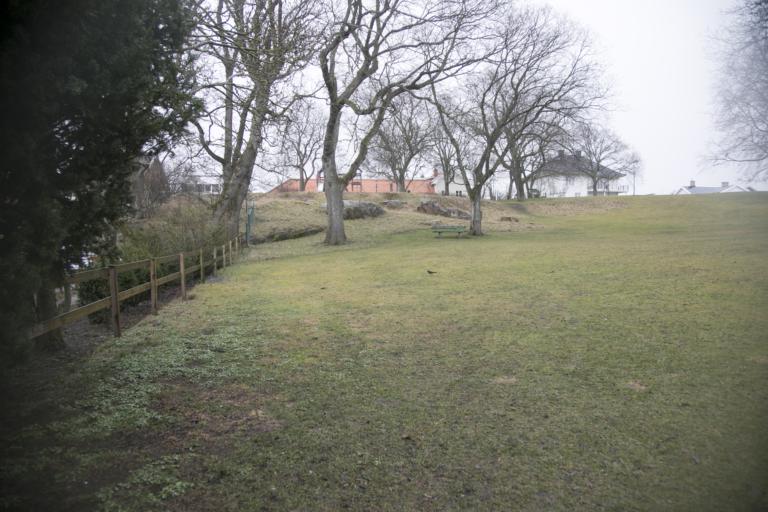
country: SE
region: Halland
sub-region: Varbergs Kommun
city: Varberg
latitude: 57.1032
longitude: 12.2493
